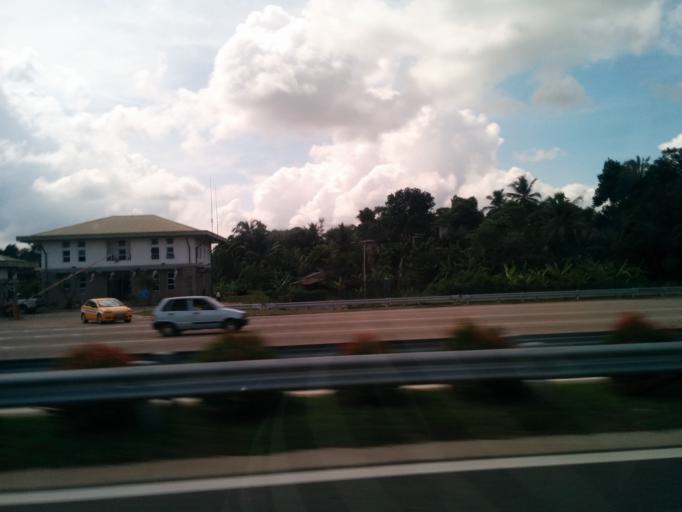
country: LK
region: Western
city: Hendala
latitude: 6.9942
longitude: 79.9036
